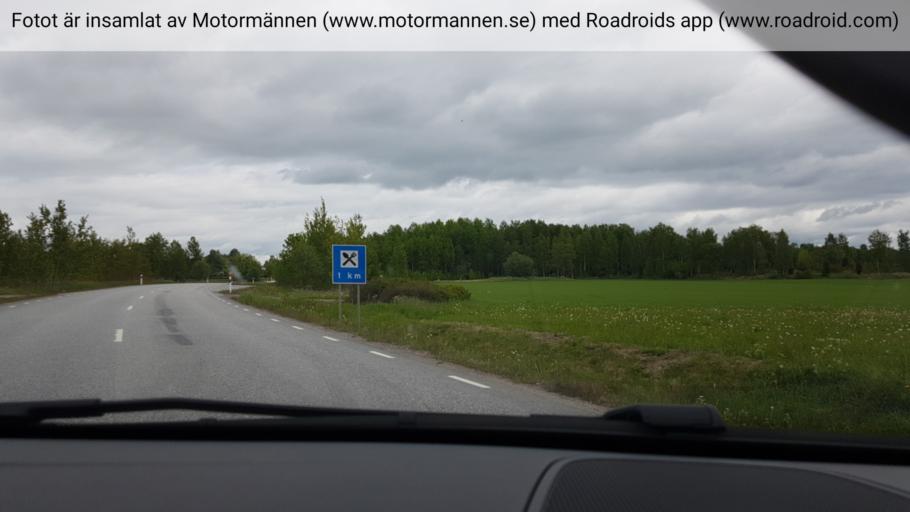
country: SE
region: Uppsala
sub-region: Heby Kommun
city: OEstervala
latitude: 60.0974
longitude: 17.1876
